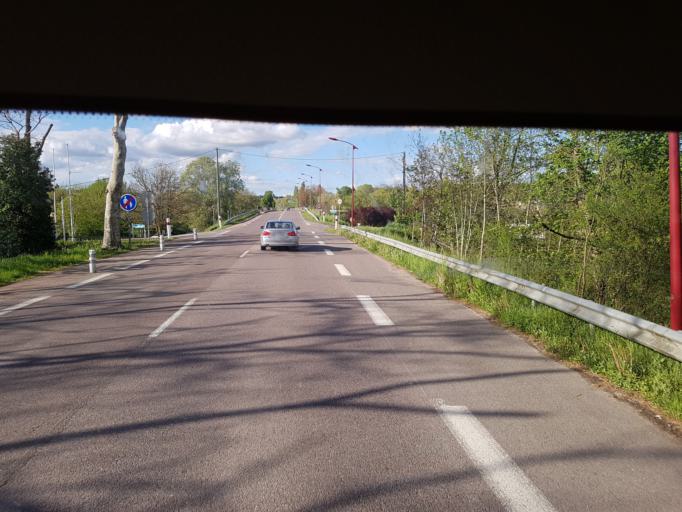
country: FR
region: Bourgogne
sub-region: Departement de l'Yonne
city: Saint-Florentin
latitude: 47.9919
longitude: 3.7344
